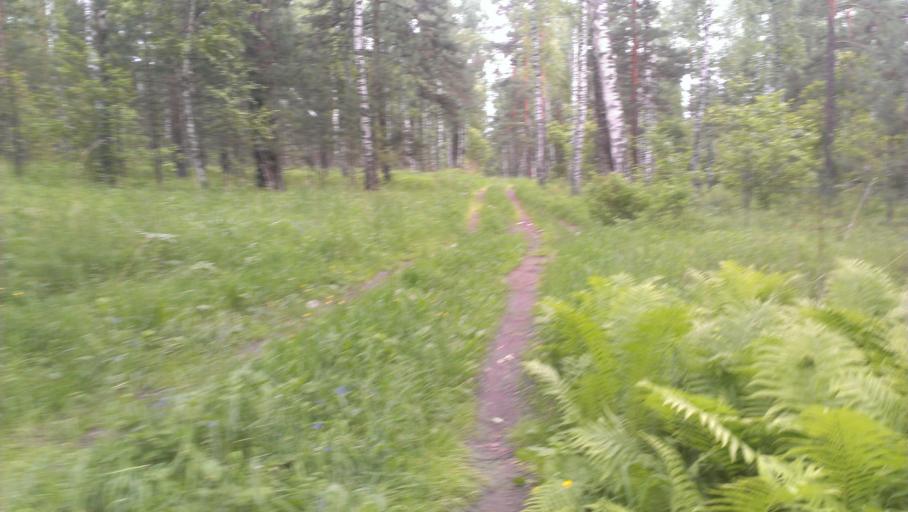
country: RU
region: Altai Krai
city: Sannikovo
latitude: 53.3459
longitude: 84.0418
